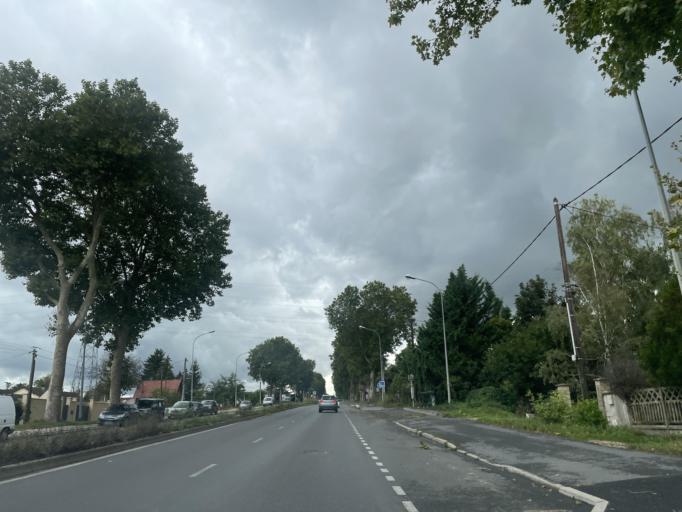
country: FR
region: Ile-de-France
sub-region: Departement de Seine-et-Marne
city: Trilport
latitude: 48.9574
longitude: 2.9312
